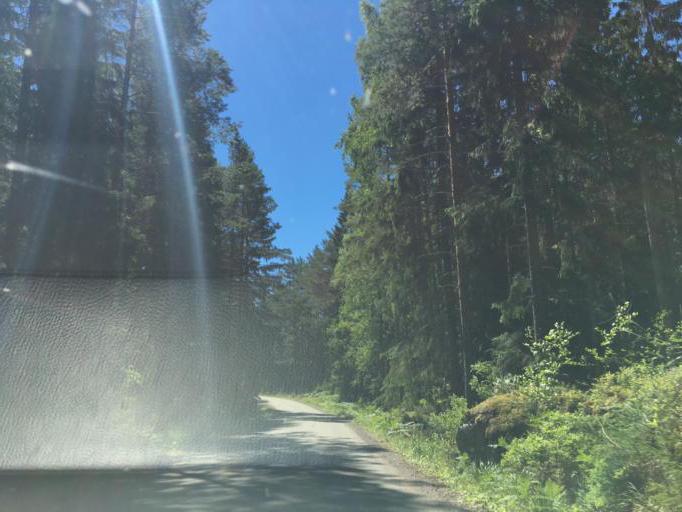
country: SE
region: Vaestra Goetaland
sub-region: Karlsborgs Kommun
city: Karlsborg
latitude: 58.7459
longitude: 14.5812
